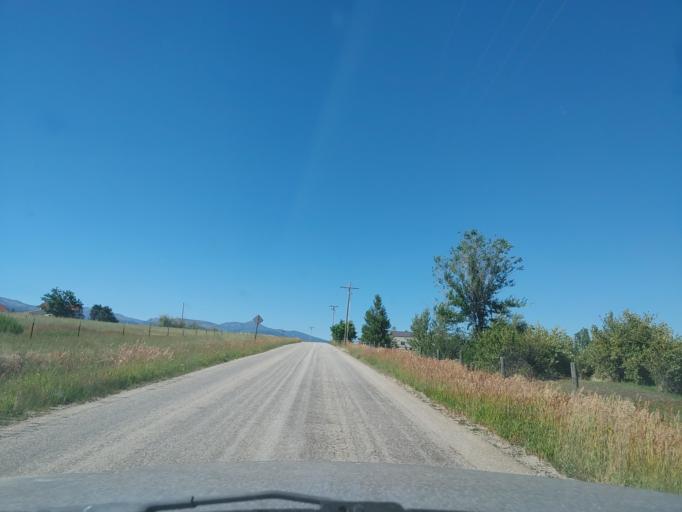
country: US
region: Montana
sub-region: Ravalli County
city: Hamilton
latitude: 46.3141
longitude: -114.2076
